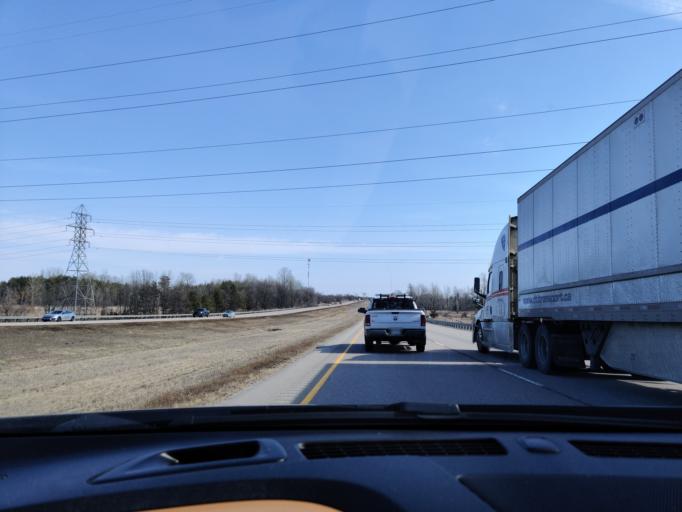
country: CA
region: Ontario
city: Kingston
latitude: 44.2861
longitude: -76.6433
